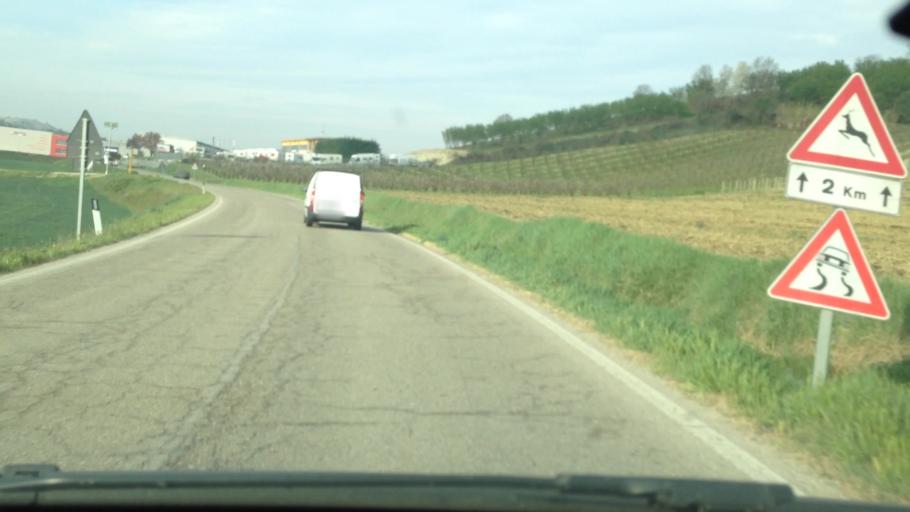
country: IT
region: Piedmont
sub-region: Provincia di Cuneo
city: Castellinaldo
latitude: 44.8083
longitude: 8.0346
